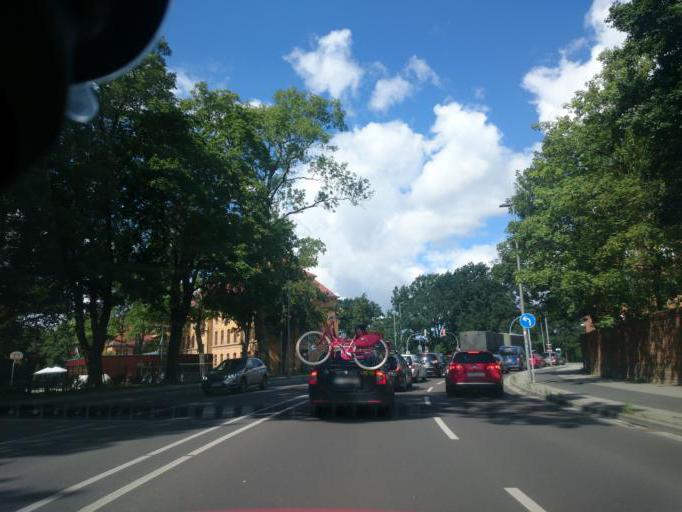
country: DE
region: Mecklenburg-Vorpommern
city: Stralsund
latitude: 54.3087
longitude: 13.0847
